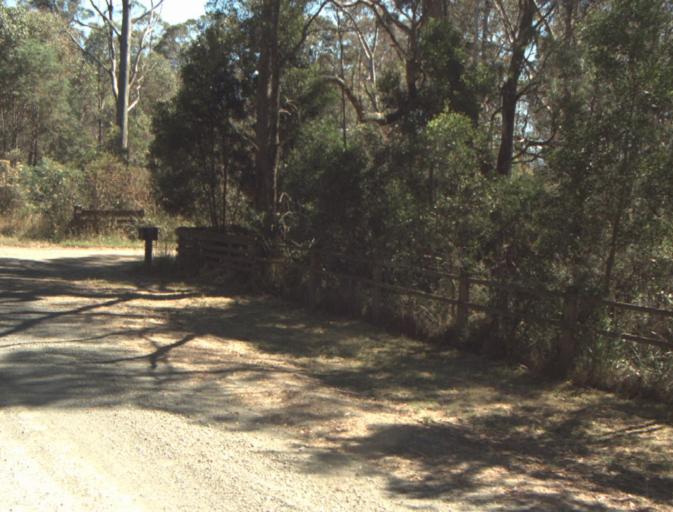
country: AU
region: Tasmania
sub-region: Launceston
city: Newstead
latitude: -41.3654
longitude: 147.2326
